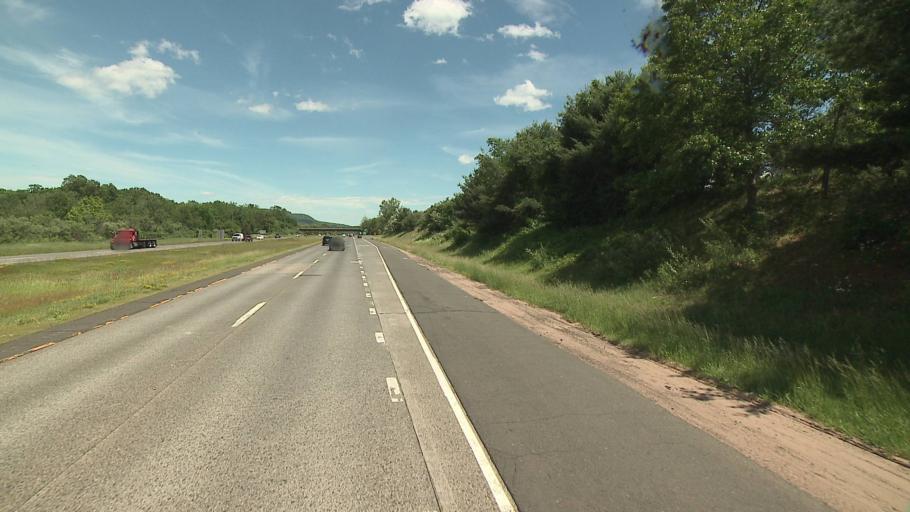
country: US
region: Connecticut
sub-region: New Haven County
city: Cheshire Village
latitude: 41.5572
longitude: -72.8964
